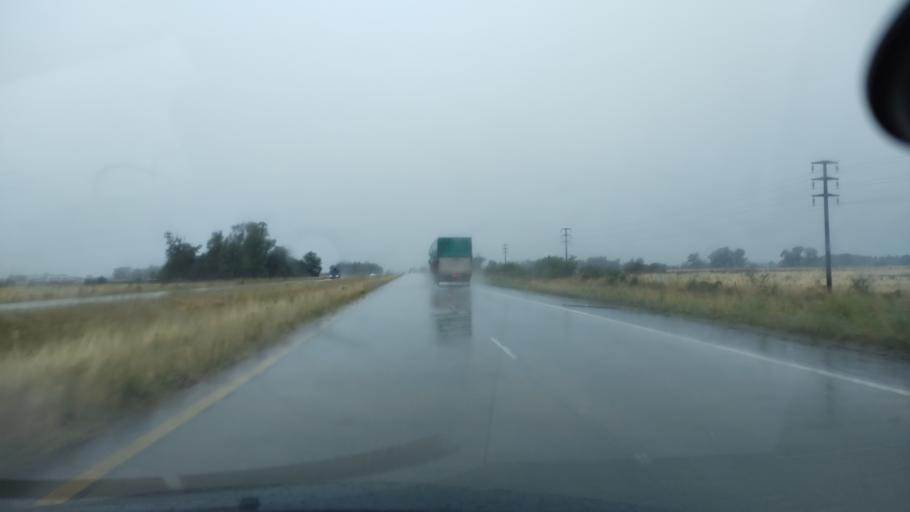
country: AR
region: Buenos Aires
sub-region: Partido de San Vicente
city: San Vicente
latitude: -35.0697
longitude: -58.5190
